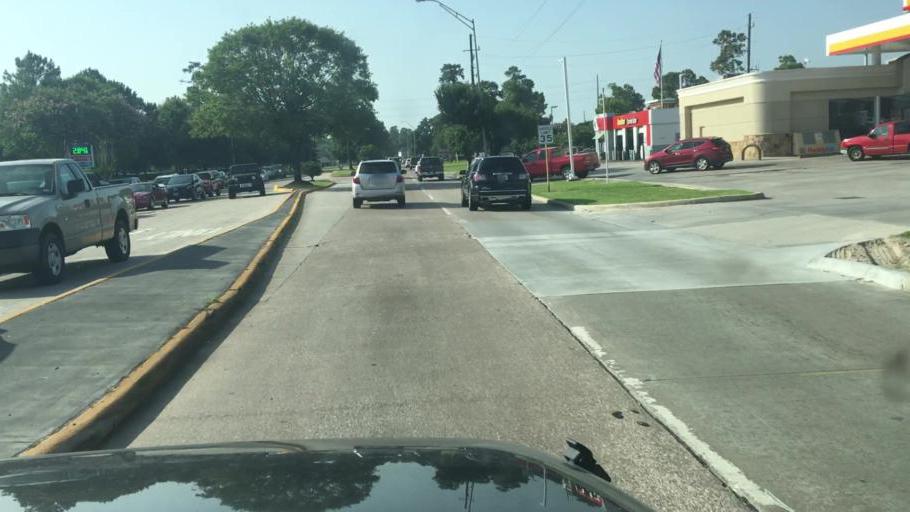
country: US
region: Texas
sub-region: Harris County
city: Atascocita
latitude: 29.9988
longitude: -95.1623
